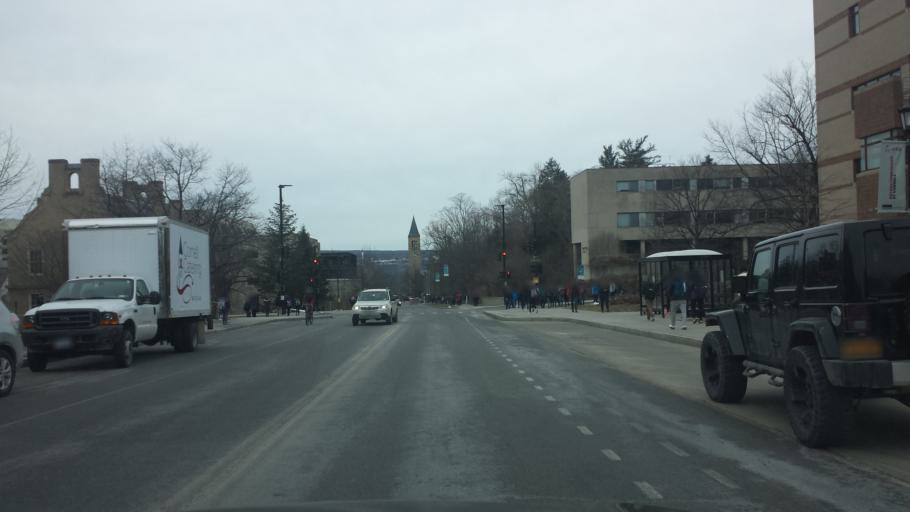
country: US
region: New York
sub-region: Tompkins County
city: East Ithaca
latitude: 42.4476
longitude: -76.4789
